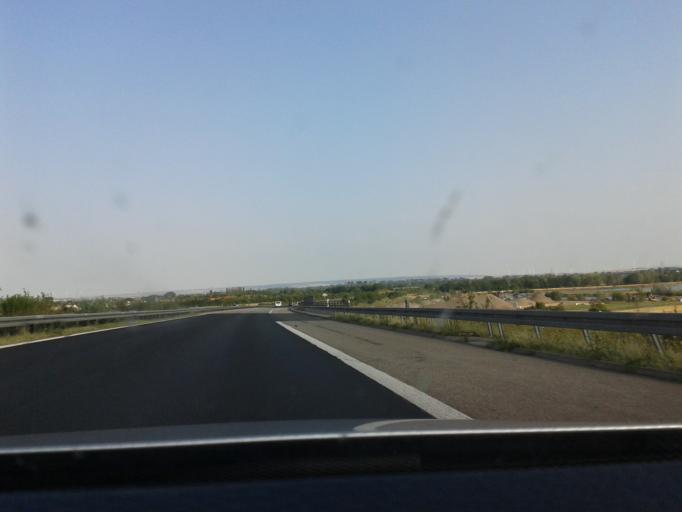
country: DE
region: Saxony-Anhalt
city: Wallhausen
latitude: 51.4618
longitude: 11.1828
